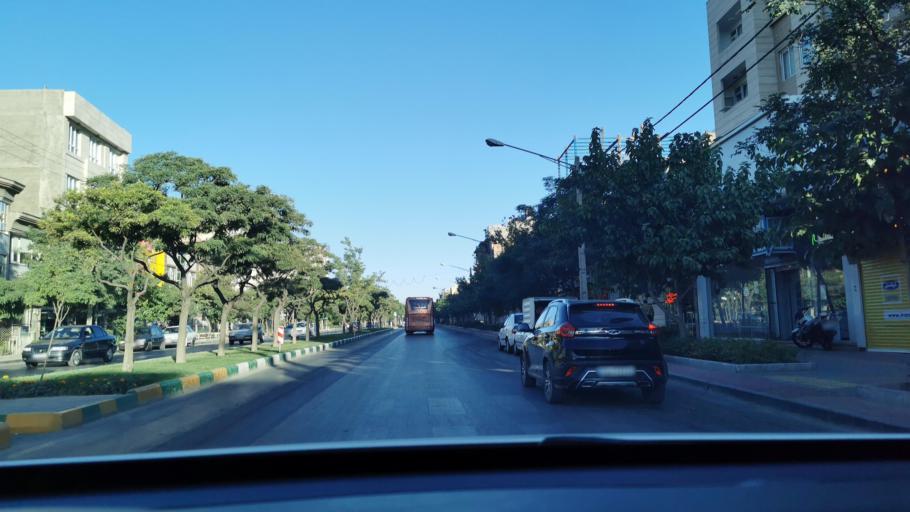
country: IR
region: Razavi Khorasan
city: Mashhad
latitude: 36.3522
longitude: 59.5006
